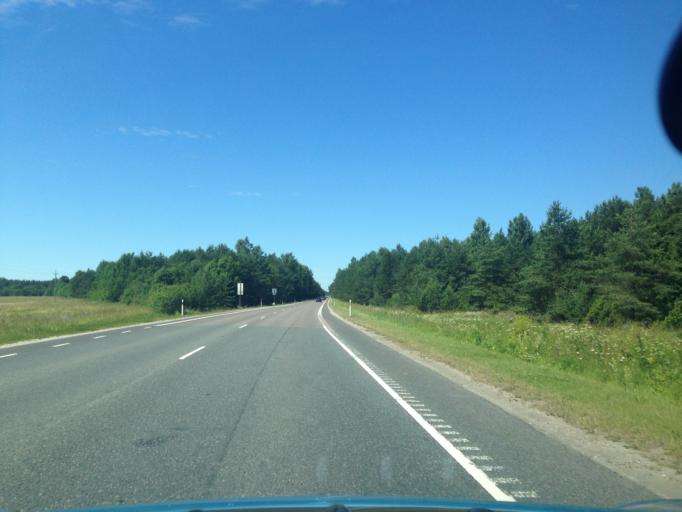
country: EE
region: Harju
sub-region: Saue linn
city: Saue
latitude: 59.3113
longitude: 24.5511
